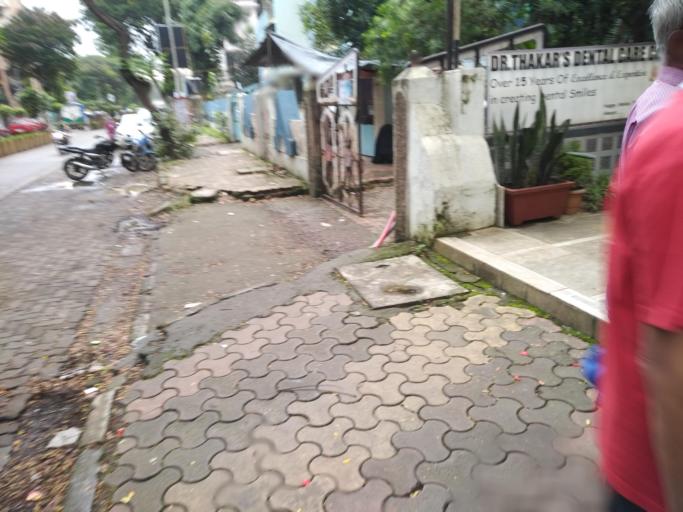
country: IN
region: Maharashtra
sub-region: Mumbai Suburban
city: Borivli
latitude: 19.2411
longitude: 72.8649
